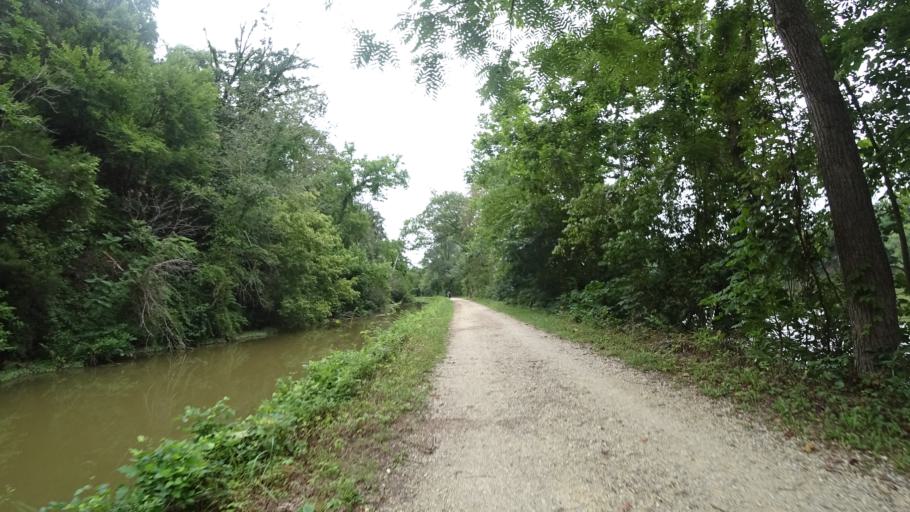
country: US
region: Maryland
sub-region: Montgomery County
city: Travilah
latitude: 39.0415
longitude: -77.2662
